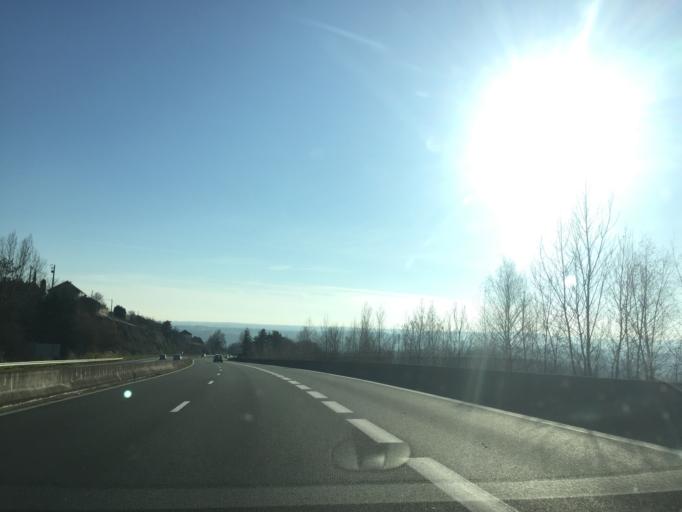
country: FR
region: Limousin
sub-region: Departement de la Correze
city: Donzenac
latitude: 45.2375
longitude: 1.5127
